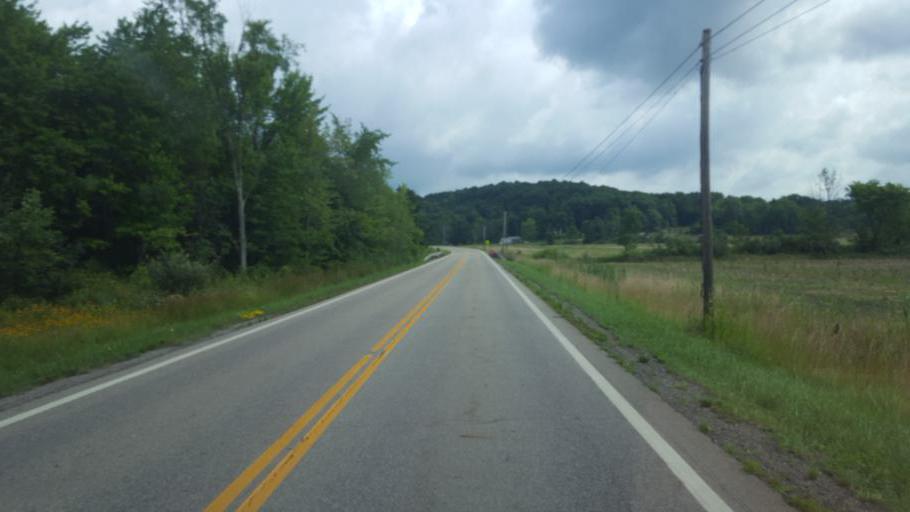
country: US
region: Ohio
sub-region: Columbiana County
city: Salineville
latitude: 40.6647
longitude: -80.8068
